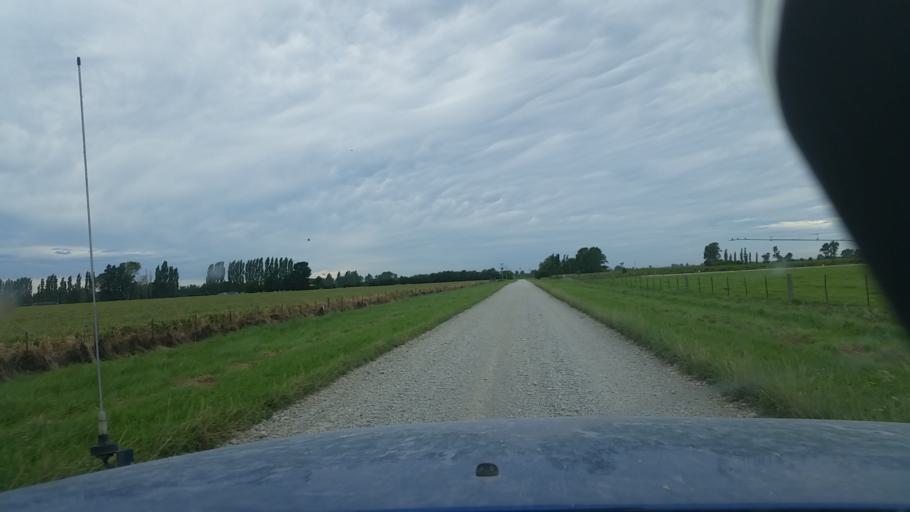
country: NZ
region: Canterbury
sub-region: Ashburton District
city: Ashburton
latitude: -43.8211
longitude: 171.6363
